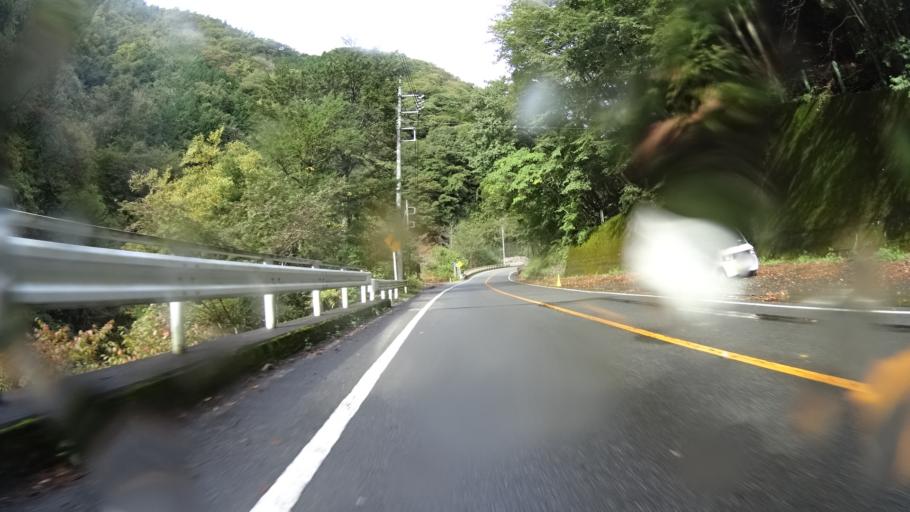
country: JP
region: Yamanashi
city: Enzan
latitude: 35.7964
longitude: 138.8974
